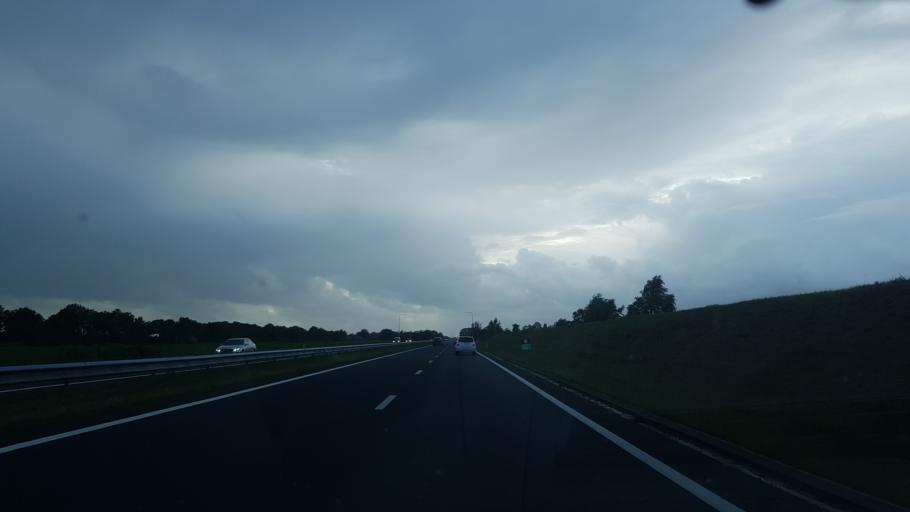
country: NL
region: Friesland
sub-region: Gemeente Smallingerland
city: Oudega
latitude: 53.1476
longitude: 5.9881
